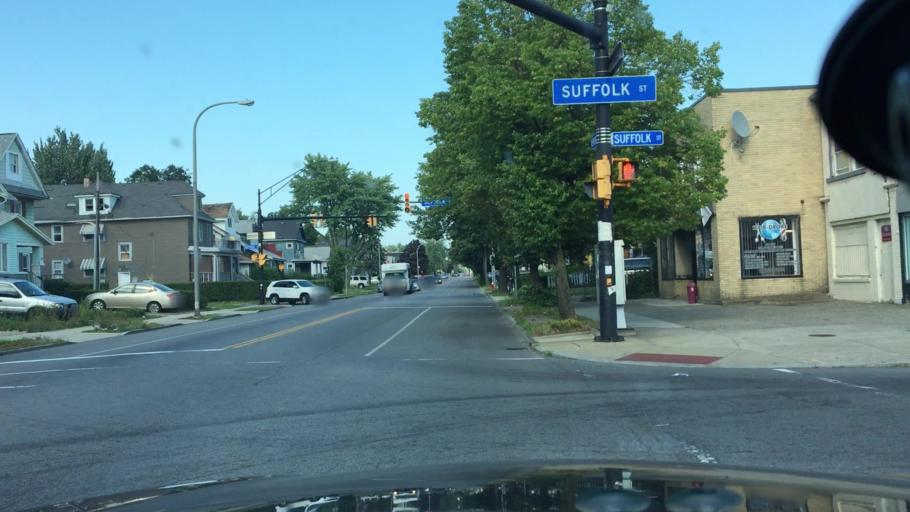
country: US
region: New York
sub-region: Erie County
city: Eggertsville
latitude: 42.9390
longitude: -78.8109
